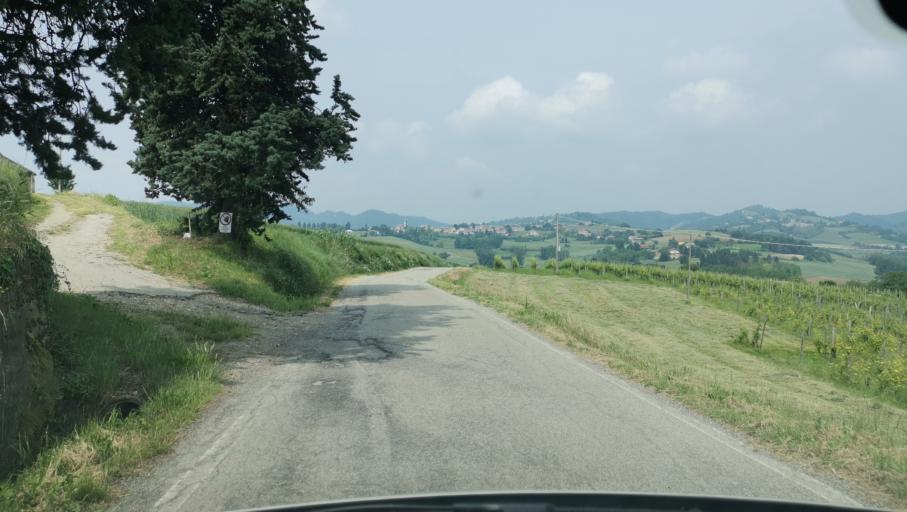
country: IT
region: Piedmont
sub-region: Provincia di Alessandria
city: Castelletto Merli
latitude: 45.0591
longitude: 8.2460
